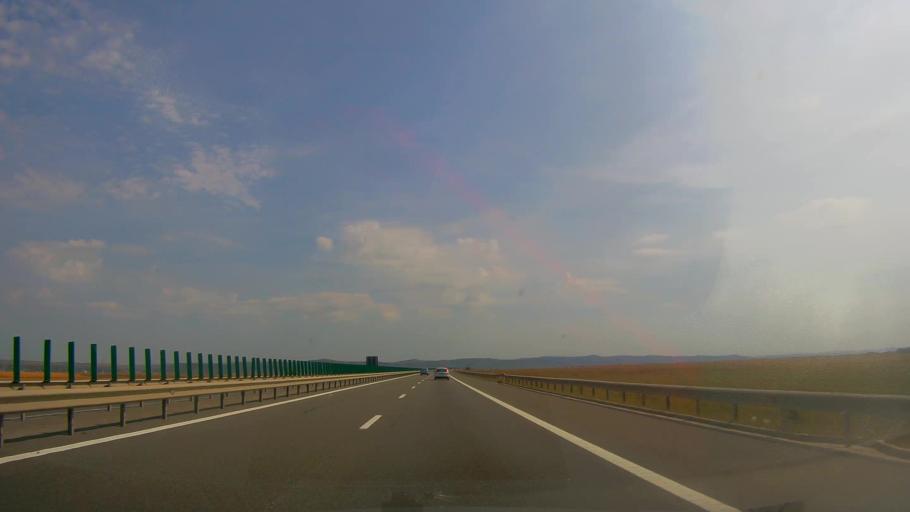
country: RO
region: Cluj
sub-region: Municipiul Campia Turzii
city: Campia Turzii
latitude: 46.5262
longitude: 23.8422
